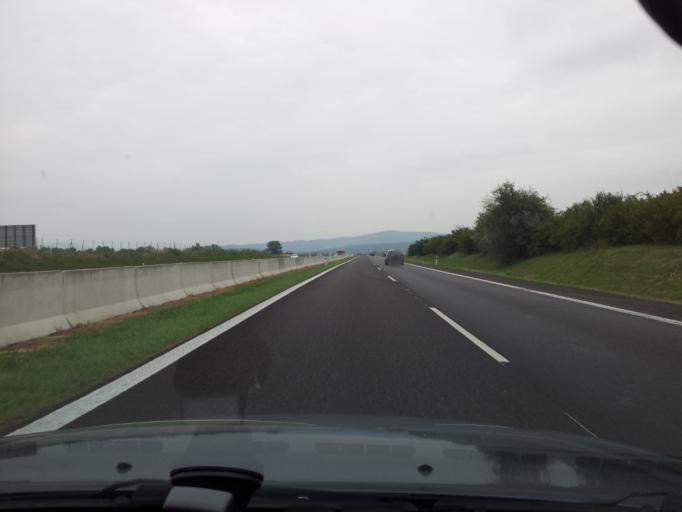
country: SK
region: Banskobystricky
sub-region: Okres Banska Bystrica
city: Zvolen
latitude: 48.6548
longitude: 19.1257
